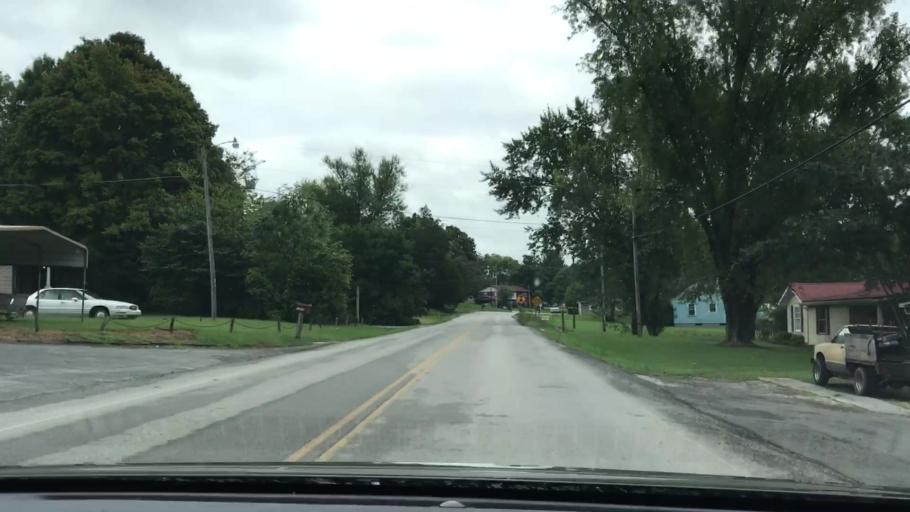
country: US
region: Kentucky
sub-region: Barren County
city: Glasgow
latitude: 36.9631
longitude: -85.8685
